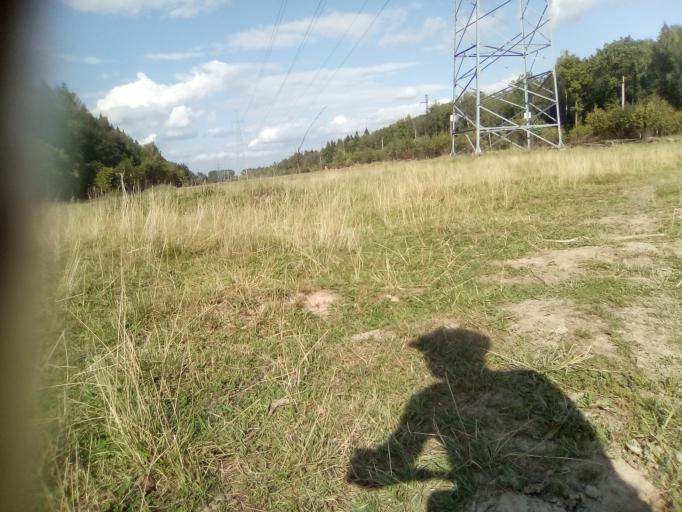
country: RU
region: Moskovskaya
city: Kokoshkino
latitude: 55.6166
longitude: 37.1731
